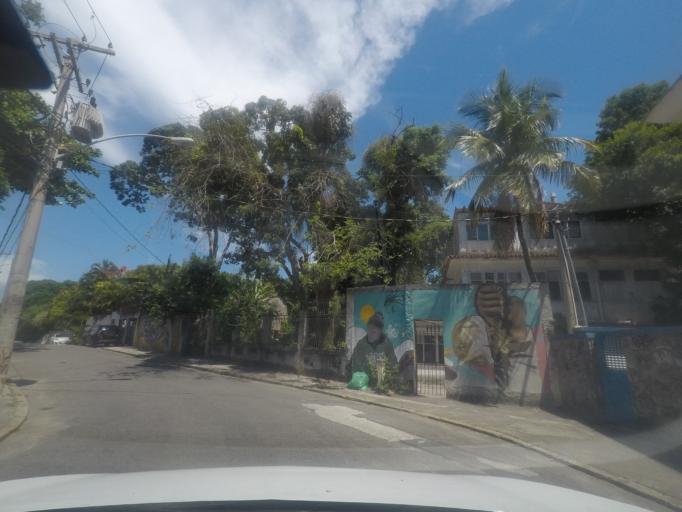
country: BR
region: Rio de Janeiro
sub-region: Itaguai
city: Itaguai
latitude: -23.0053
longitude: -43.6389
